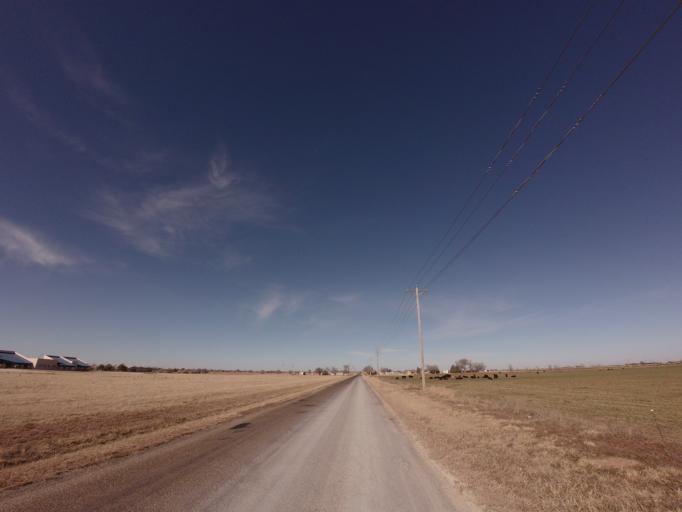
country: US
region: New Mexico
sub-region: Curry County
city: Clovis
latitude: 34.4023
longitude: -103.1611
